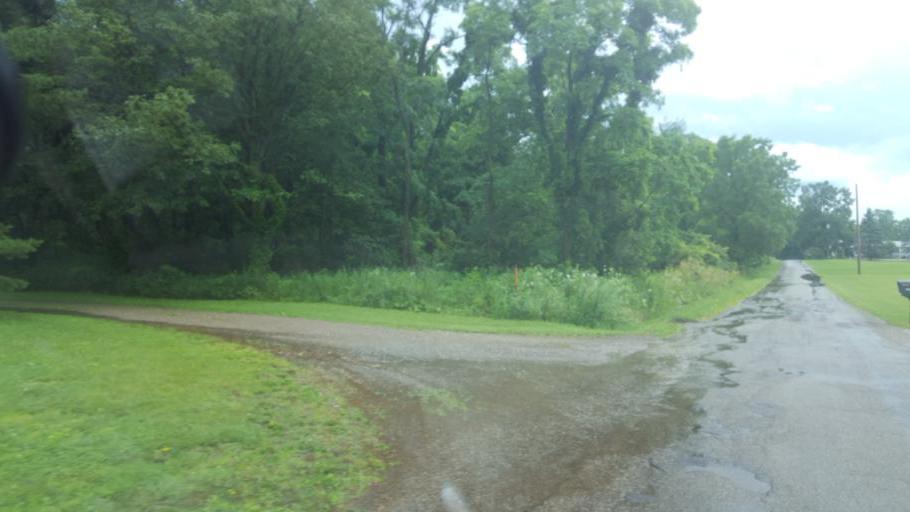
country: US
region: Ohio
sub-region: Richland County
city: Lexington
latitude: 40.6693
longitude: -82.6388
